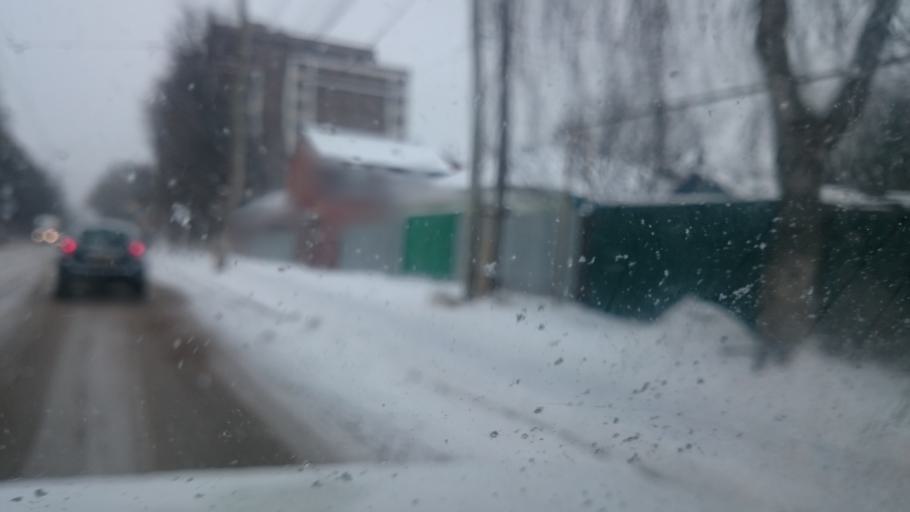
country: RU
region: Tula
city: Mendeleyevskiy
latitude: 54.1657
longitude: 37.5956
